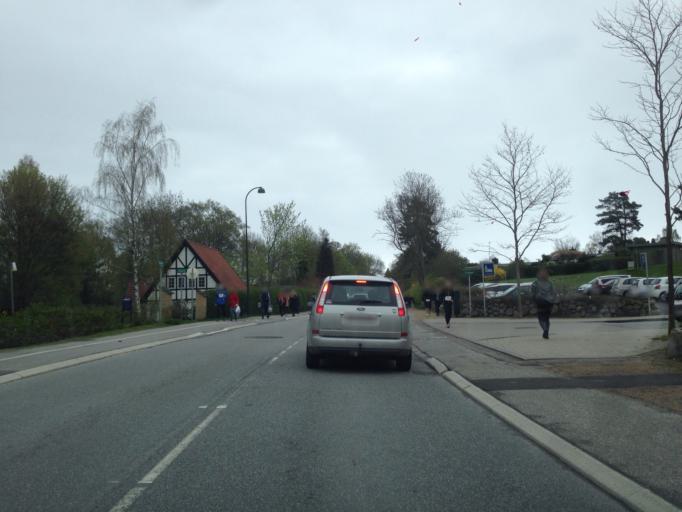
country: DK
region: Capital Region
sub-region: Rudersdal Kommune
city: Trorod
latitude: 55.8216
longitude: 12.5355
